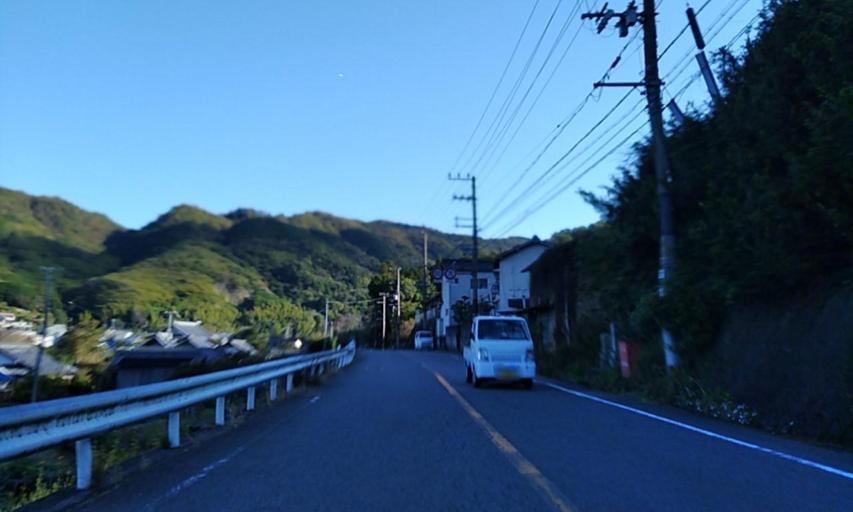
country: JP
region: Wakayama
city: Iwade
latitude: 34.1533
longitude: 135.3186
